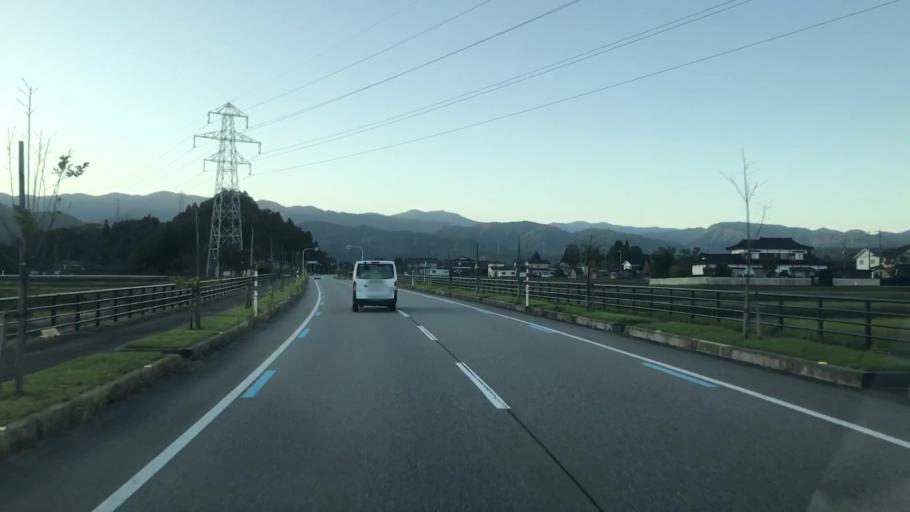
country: JP
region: Toyama
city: Kamiichi
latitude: 36.6105
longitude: 137.3245
